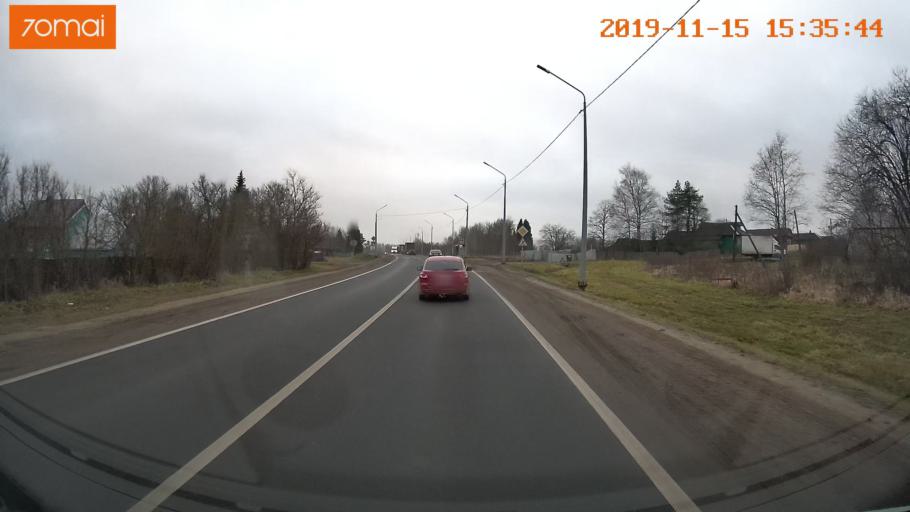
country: RU
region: Jaroslavl
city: Danilov
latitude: 58.0560
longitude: 40.0878
